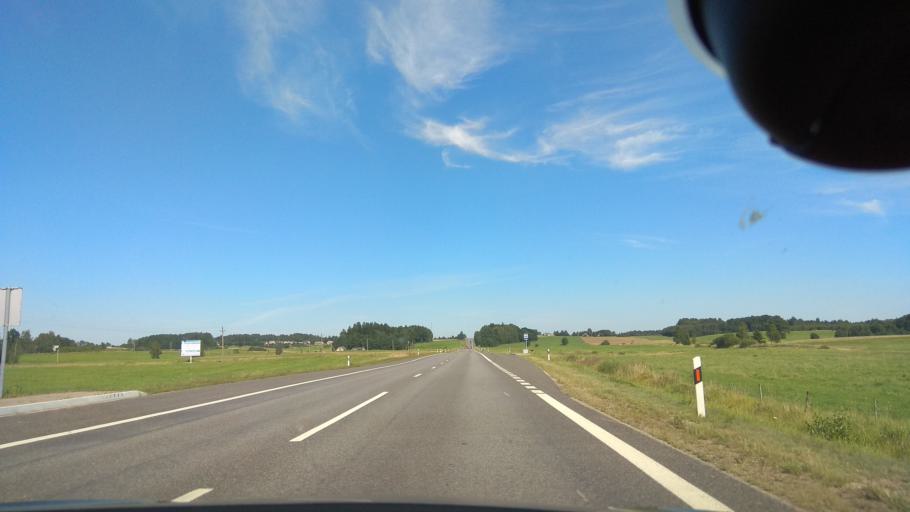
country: LT
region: Telsiu apskritis
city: Plunge
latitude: 55.9640
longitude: 21.9820
